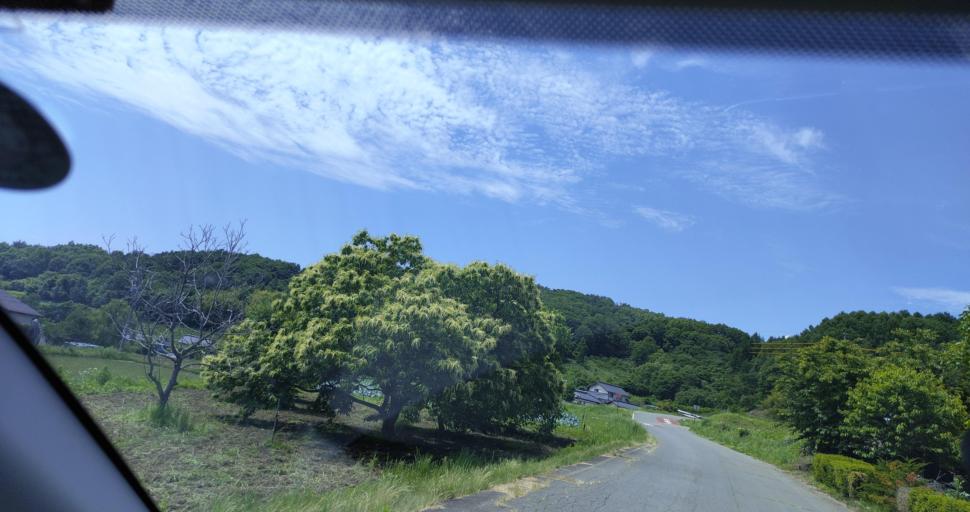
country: JP
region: Nagano
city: Ueda
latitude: 36.3909
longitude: 138.3331
